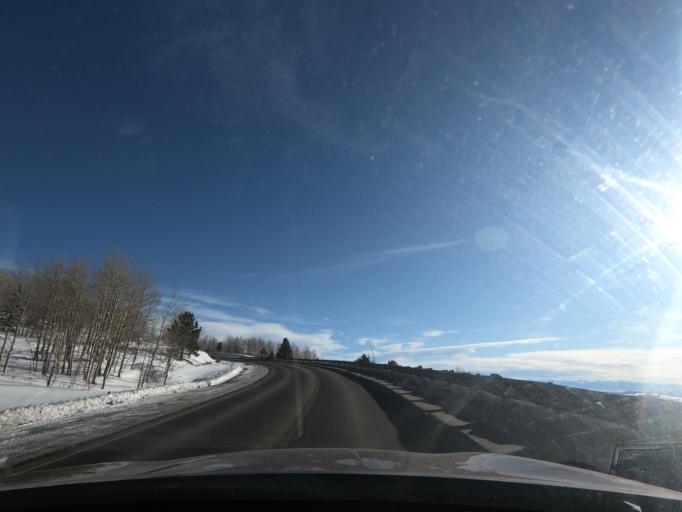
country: US
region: Colorado
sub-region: Teller County
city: Cripple Creek
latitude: 38.7524
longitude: -105.1654
